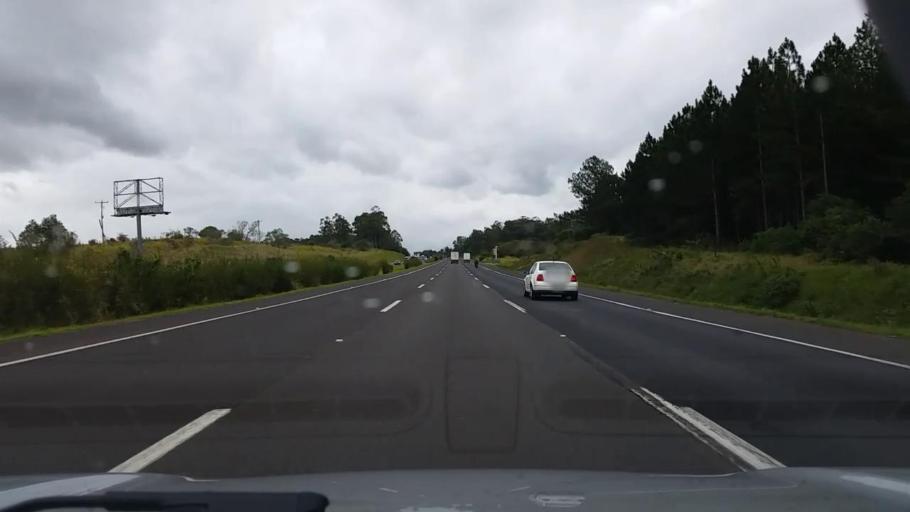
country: BR
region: Rio Grande do Sul
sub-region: Gravatai
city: Gravatai
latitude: -29.9265
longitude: -50.8665
